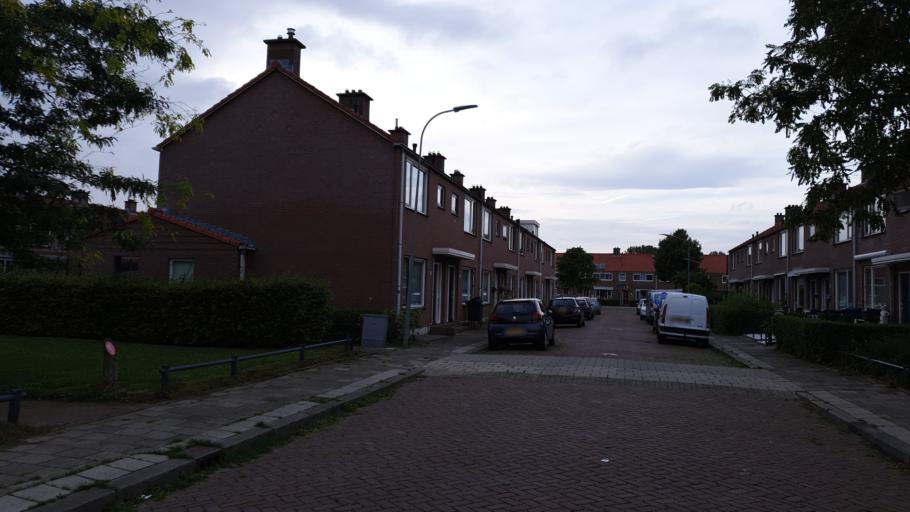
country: NL
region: South Holland
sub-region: Gemeente Dordrecht
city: Dordrecht
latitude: 51.8007
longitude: 4.6675
